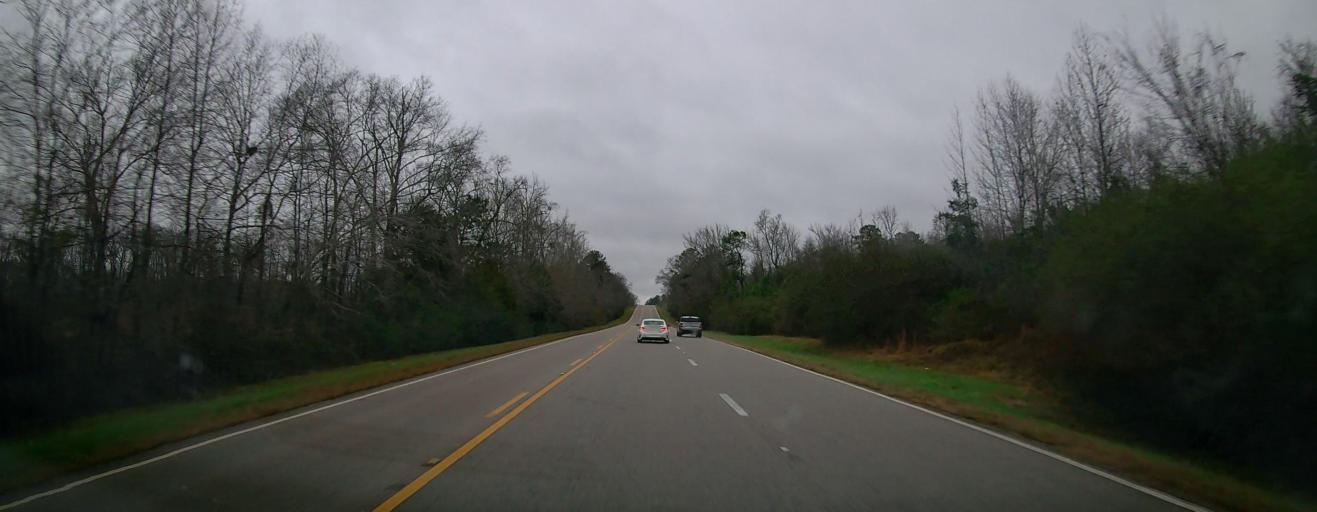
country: US
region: Alabama
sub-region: Bibb County
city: Centreville
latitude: 32.8505
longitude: -86.9623
